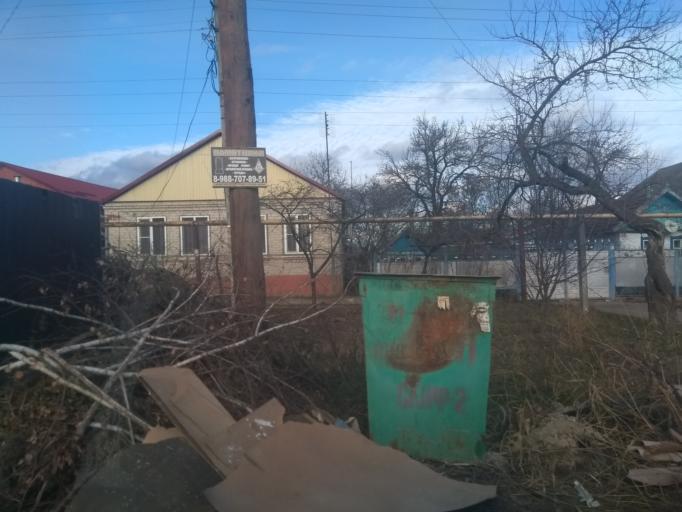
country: RU
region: Stavropol'skiy
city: Krasnokumskoye
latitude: 44.1756
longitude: 43.4854
